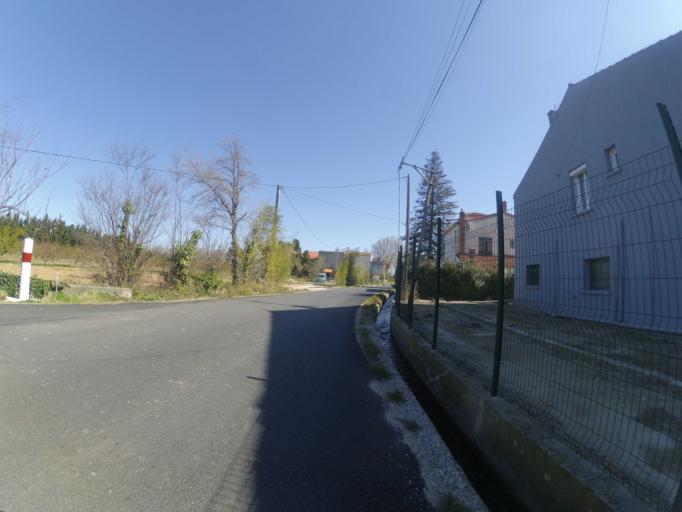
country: FR
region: Languedoc-Roussillon
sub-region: Departement des Pyrenees-Orientales
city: Ille-sur-Tet
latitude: 42.6702
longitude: 2.6504
